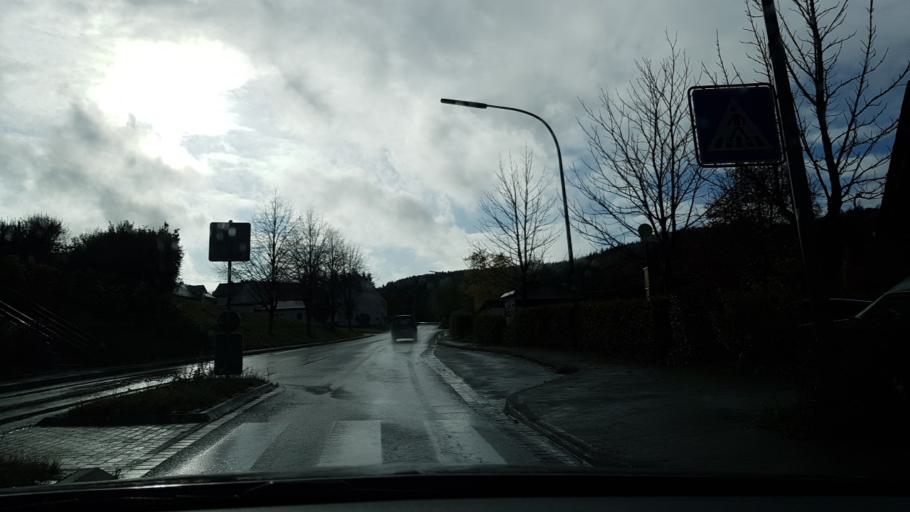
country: DE
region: Rheinland-Pfalz
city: Quiddelbach
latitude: 50.3510
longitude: 6.9374
